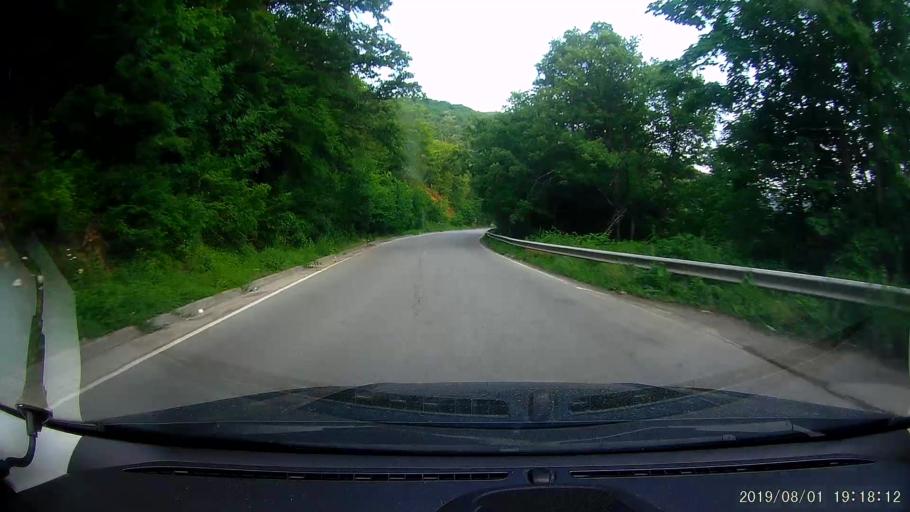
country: BG
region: Shumen
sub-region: Obshtina Smyadovo
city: Smyadovo
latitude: 42.9158
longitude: 26.9390
